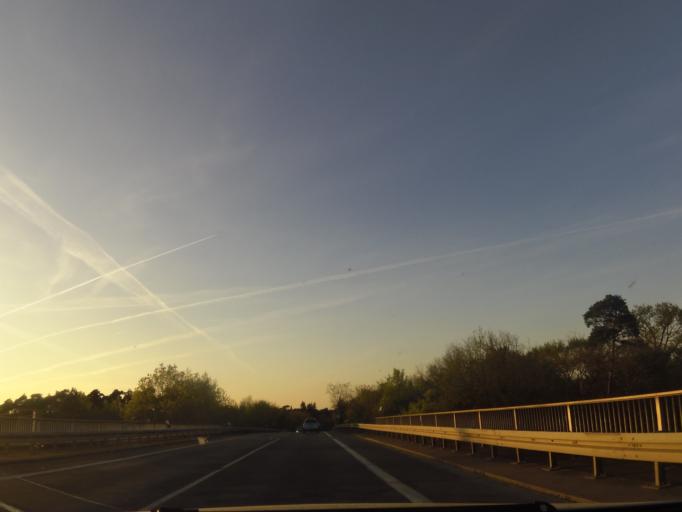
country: DE
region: Hesse
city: Weiterstadt
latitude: 49.9010
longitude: 8.6177
